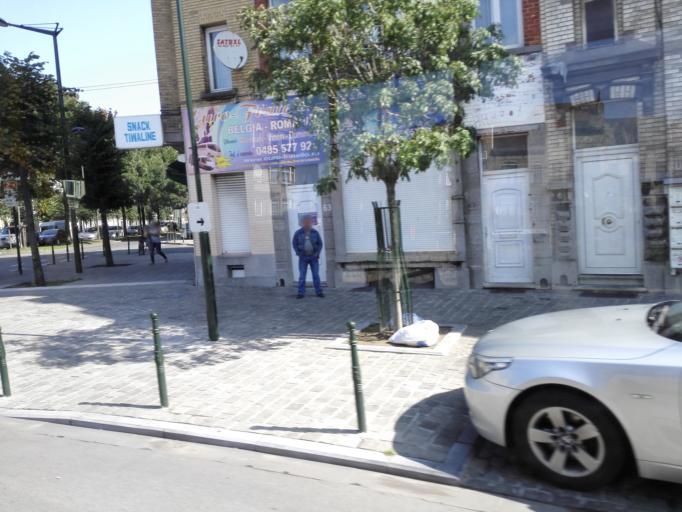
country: BE
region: Brussels Capital
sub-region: Bruxelles-Capitale
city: Brussels
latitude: 50.8716
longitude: 4.3449
